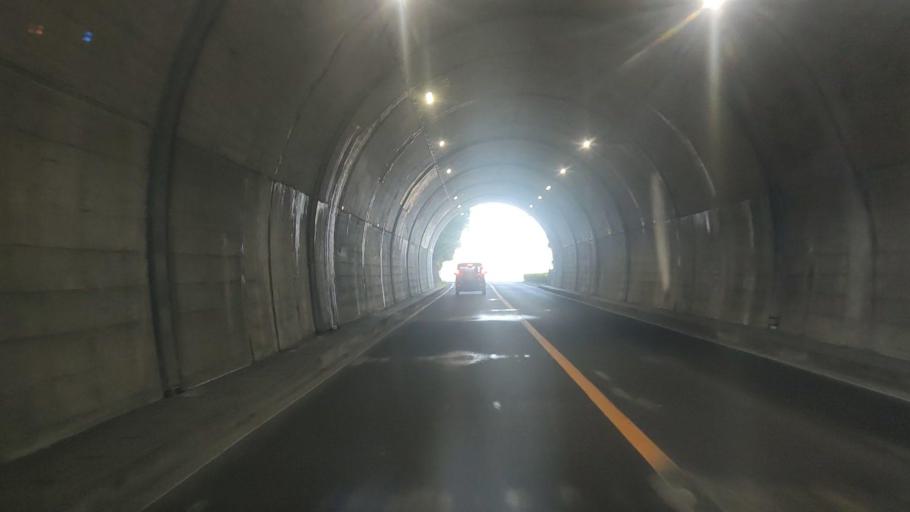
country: JP
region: Oita
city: Saiki
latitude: 32.9426
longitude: 131.9087
